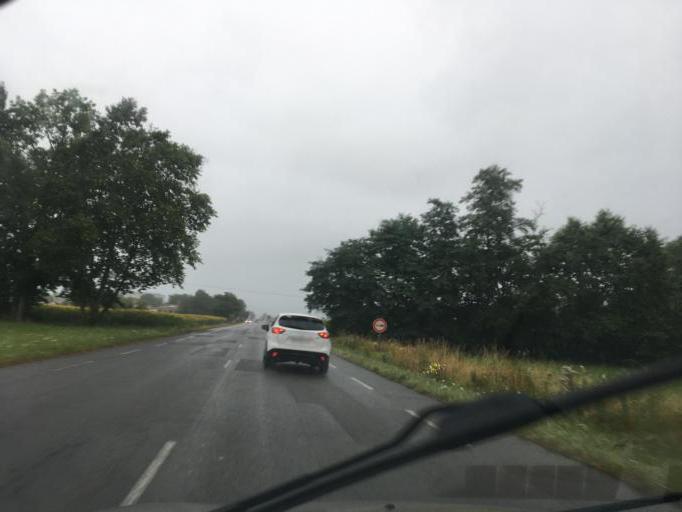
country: FR
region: Midi-Pyrenees
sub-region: Departement des Hautes-Pyrenees
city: Bazet
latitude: 43.2832
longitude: 0.0697
